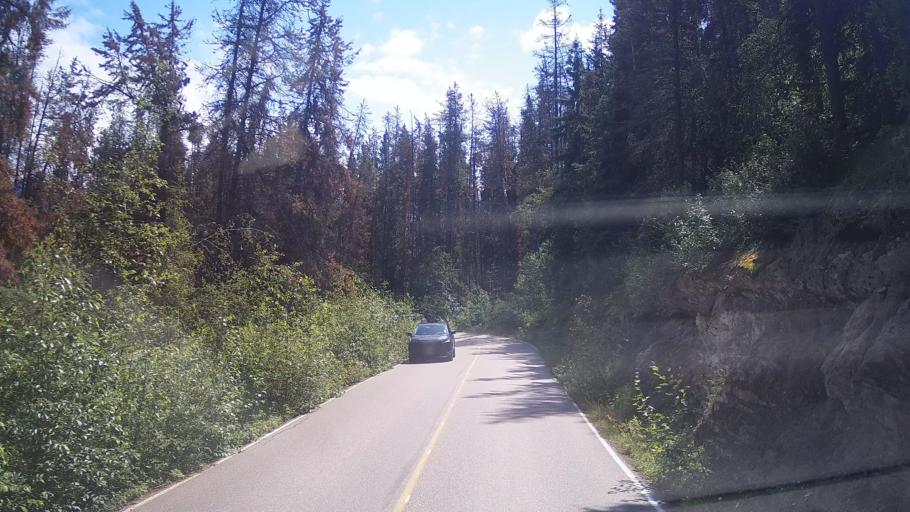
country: CA
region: Alberta
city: Jasper Park Lodge
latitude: 52.7674
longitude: -118.0268
